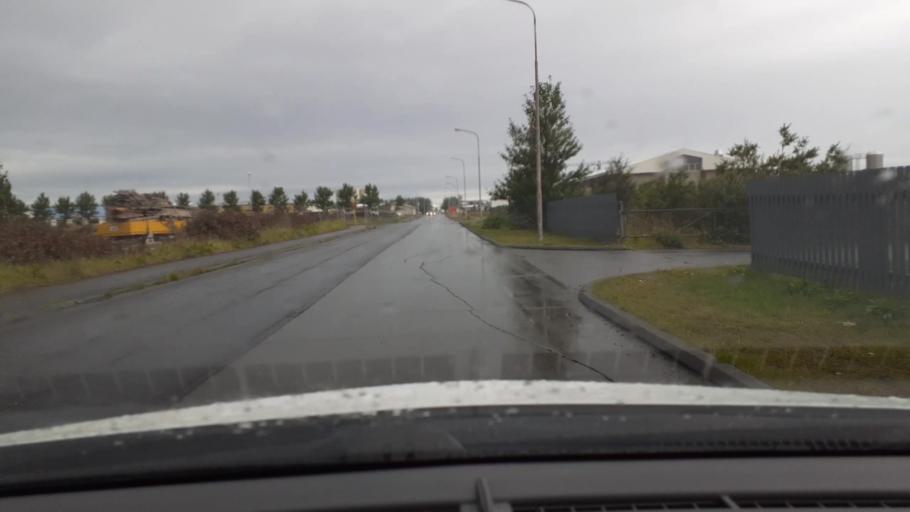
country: IS
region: West
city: Akranes
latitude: 64.3256
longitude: -22.0601
